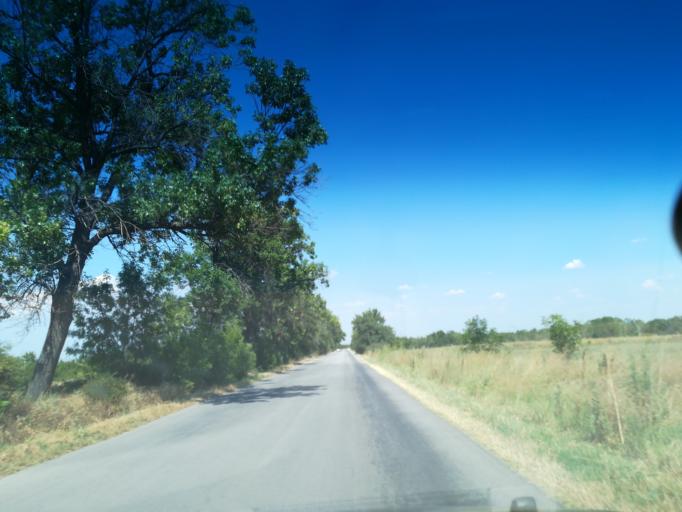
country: BG
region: Stara Zagora
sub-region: Obshtina Chirpan
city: Chirpan
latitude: 42.0646
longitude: 25.1704
